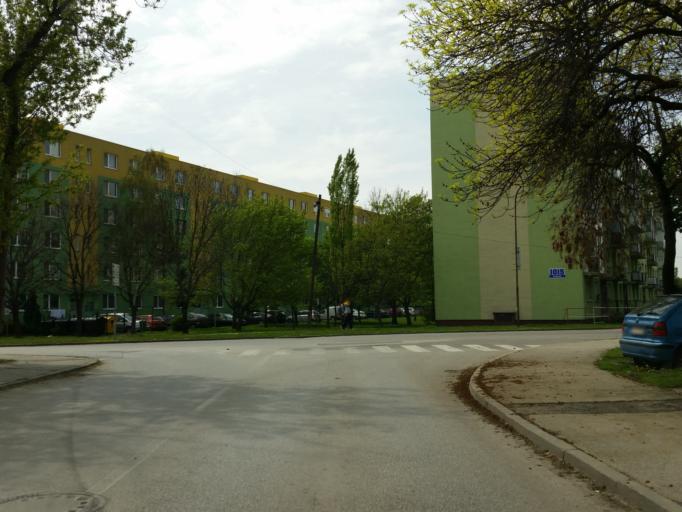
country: SK
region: Trnavsky
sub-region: Okres Galanta
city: Galanta
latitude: 48.2862
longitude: 17.7332
